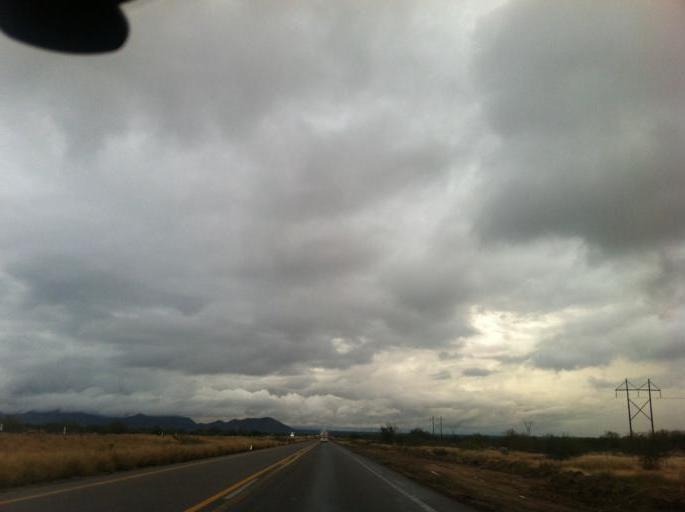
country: MX
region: Sonora
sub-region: San Miguel de Horcasitas
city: Las Mercedes [Agropecuaria]
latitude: 29.5148
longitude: -111.0050
